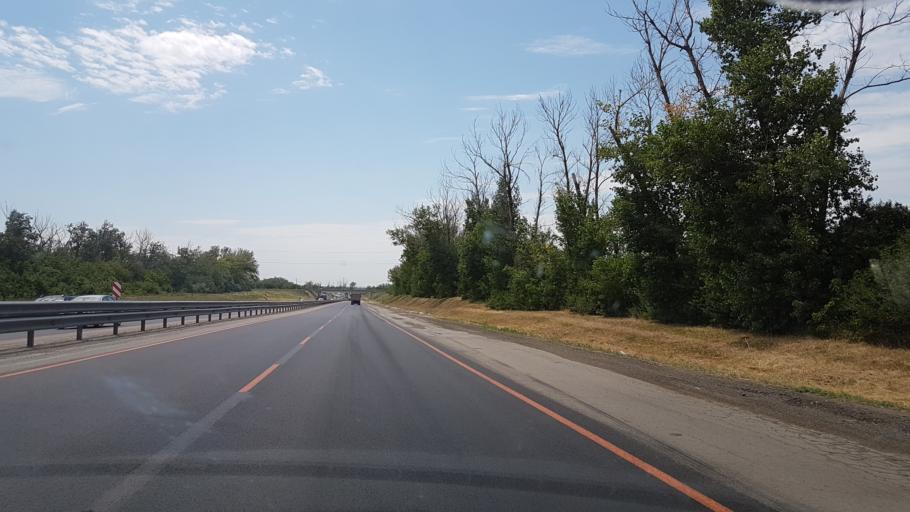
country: RU
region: Rostov
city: Gornyy
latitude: 47.8475
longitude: 40.1927
